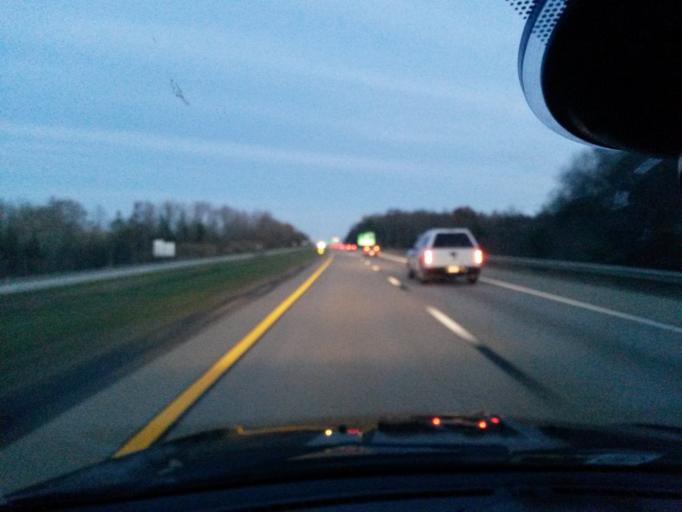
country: US
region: West Virginia
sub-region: Raleigh County
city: Daniels
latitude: 37.7737
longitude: -81.0841
